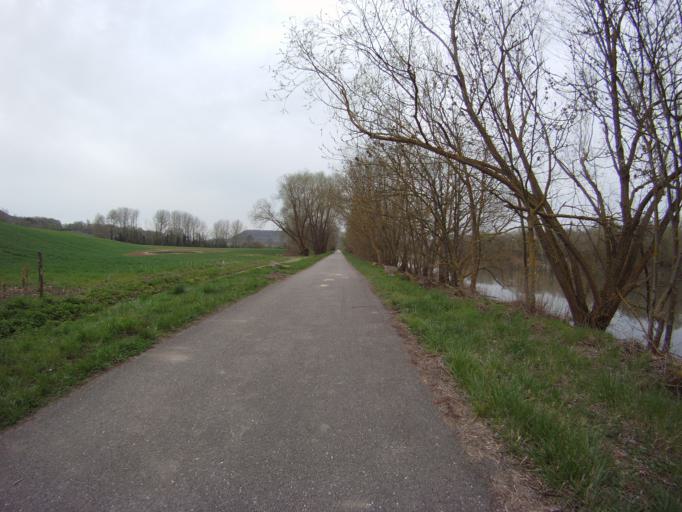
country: FR
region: Lorraine
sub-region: Departement de Meurthe-et-Moselle
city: Bouxieres-aux-Dames
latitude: 48.7425
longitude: 6.1799
